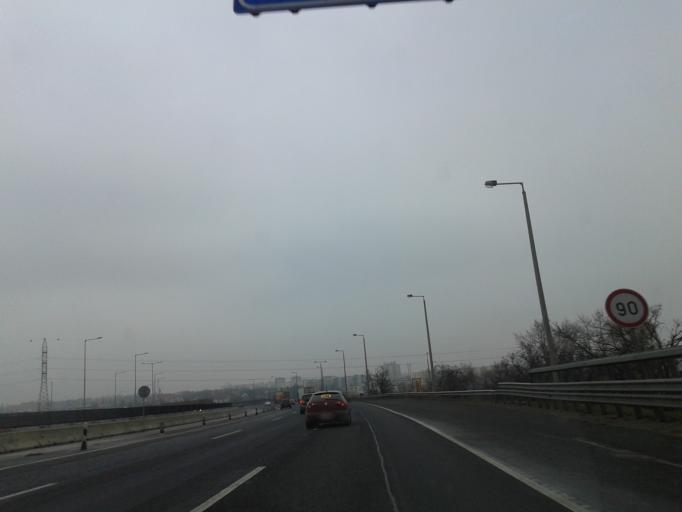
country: HU
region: Budapest
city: Budapest XXII. keruelet
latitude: 47.3970
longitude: 19.0117
